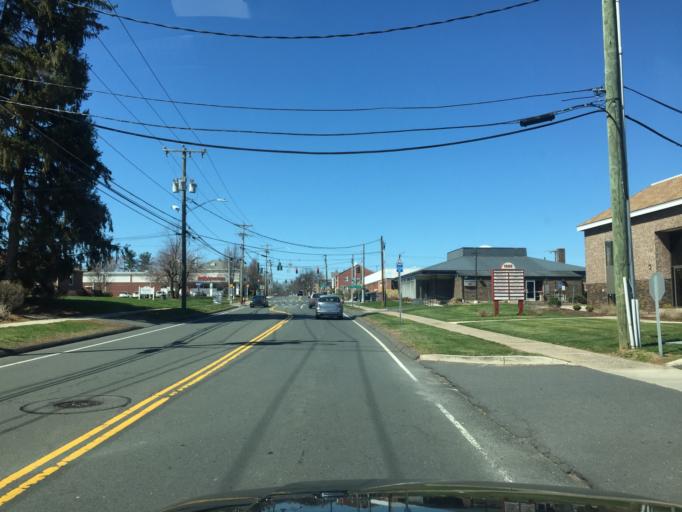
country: US
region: Connecticut
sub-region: Hartford County
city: Newington
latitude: 41.6943
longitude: -72.7225
